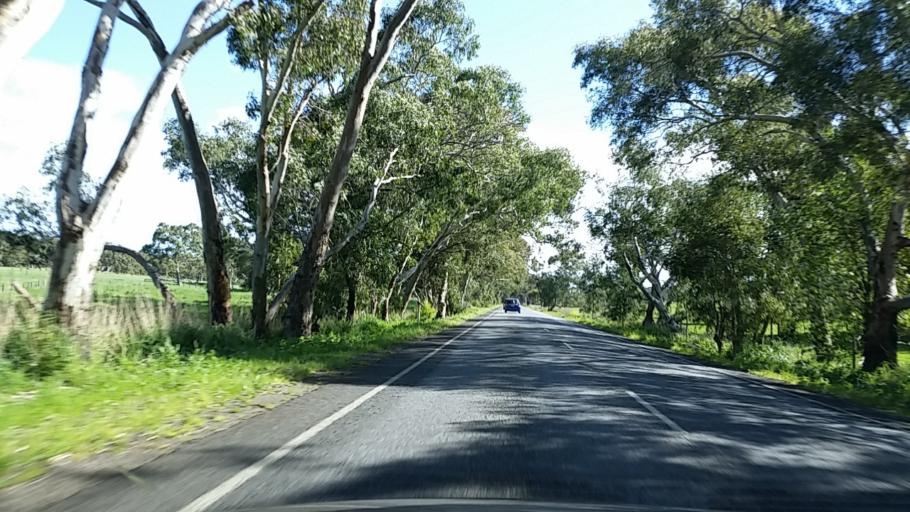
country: AU
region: South Australia
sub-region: Alexandrina
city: Mount Compass
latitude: -35.2857
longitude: 138.6109
